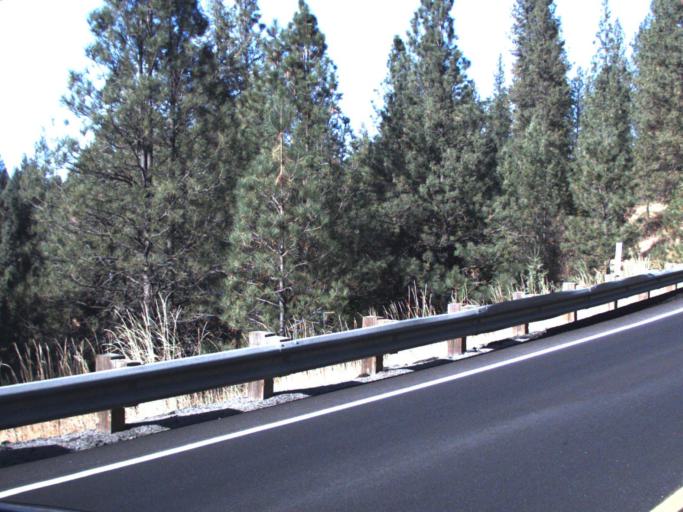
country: US
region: Washington
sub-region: Lincoln County
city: Davenport
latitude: 48.0285
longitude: -118.2324
